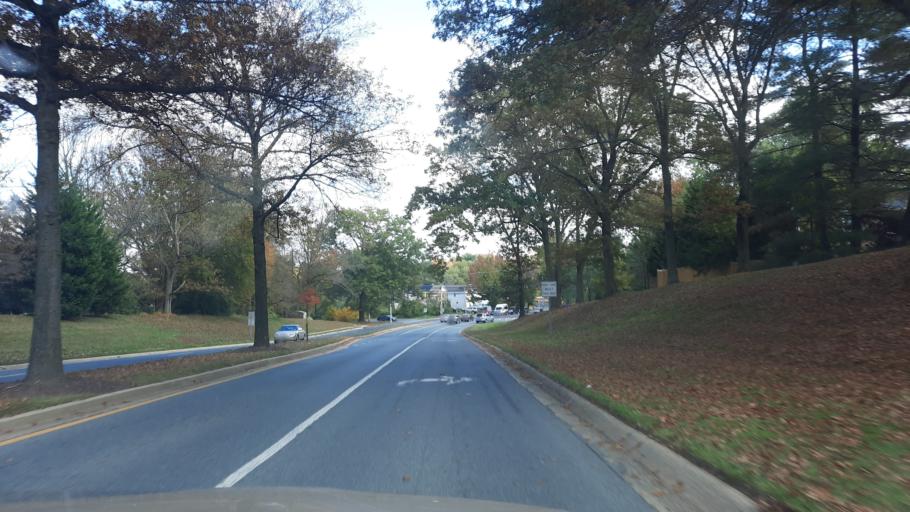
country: US
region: Maryland
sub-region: Montgomery County
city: Montgomery Village
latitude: 39.1694
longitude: -77.1926
